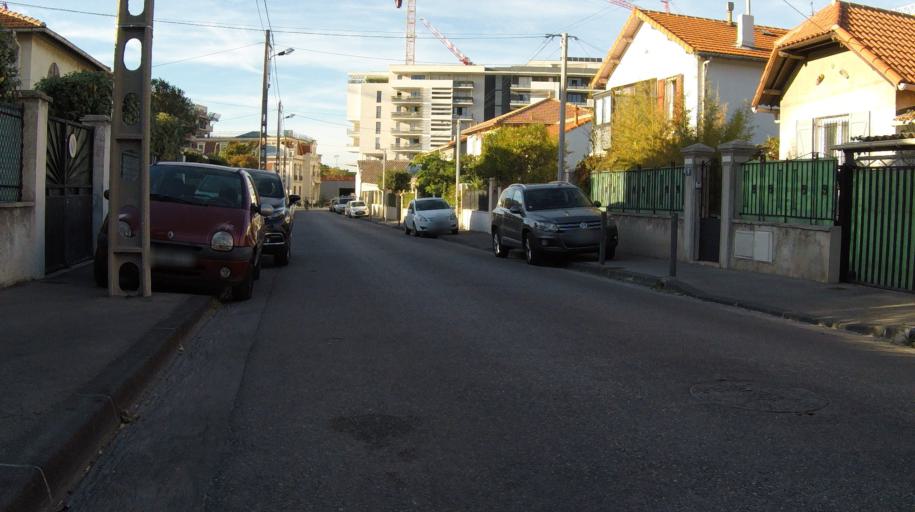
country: FR
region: Provence-Alpes-Cote d'Azur
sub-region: Departement des Bouches-du-Rhone
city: Marseille 10
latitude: 43.2804
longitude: 5.4243
